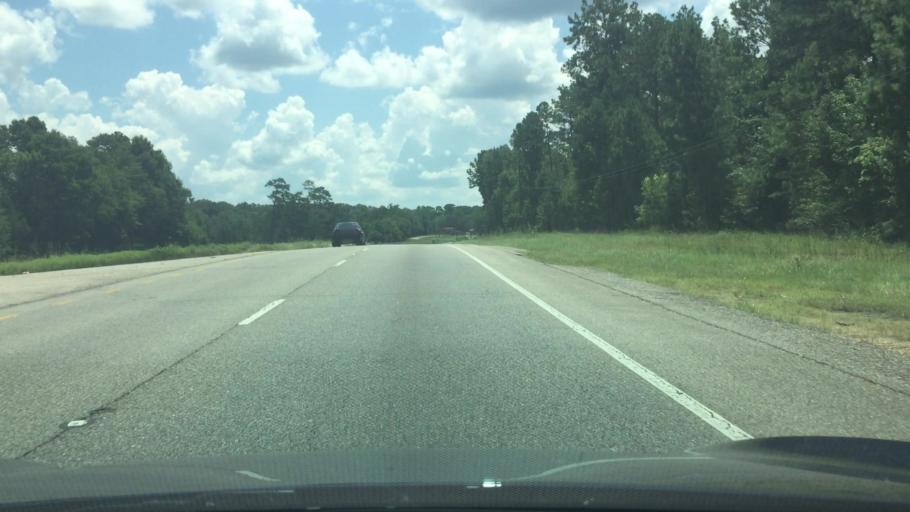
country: US
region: Alabama
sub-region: Montgomery County
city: Pike Road
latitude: 32.1201
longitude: -86.0724
